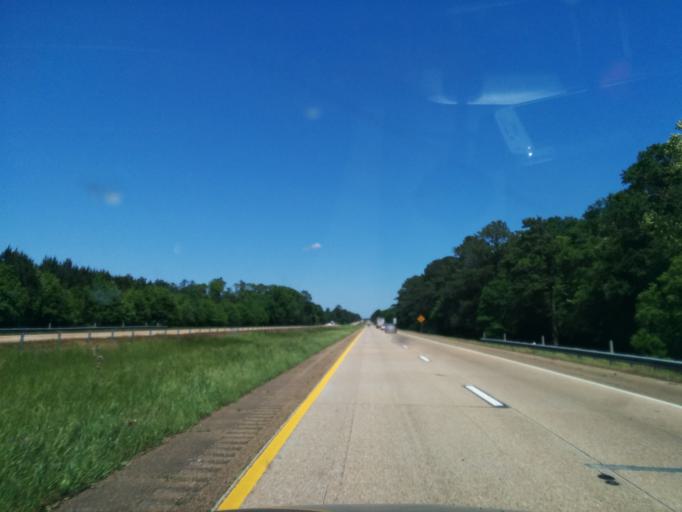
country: US
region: Mississippi
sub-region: Pike County
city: Magnolia
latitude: 31.1168
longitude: -90.4843
